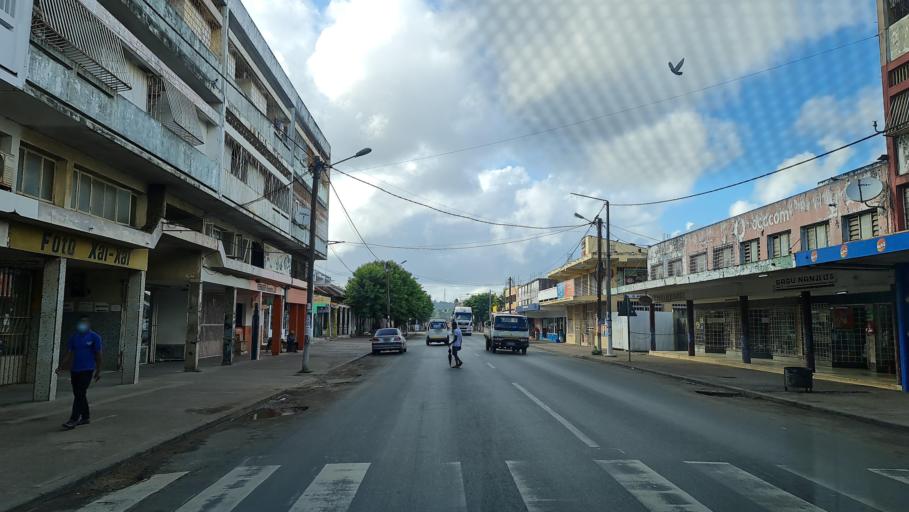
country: MZ
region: Gaza
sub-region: Xai-Xai District
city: Xai-Xai
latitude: -25.0440
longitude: 33.6426
